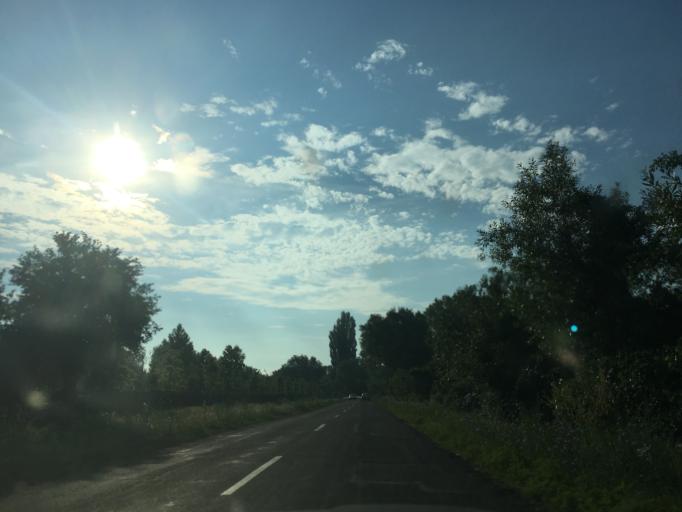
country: HU
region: Hajdu-Bihar
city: Debrecen
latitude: 47.5455
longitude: 21.7102
